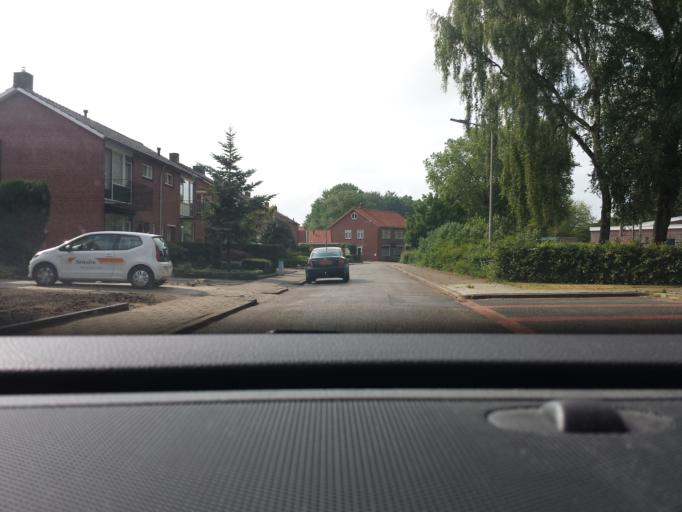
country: NL
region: Gelderland
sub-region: Berkelland
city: Borculo
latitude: 52.0661
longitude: 6.5618
